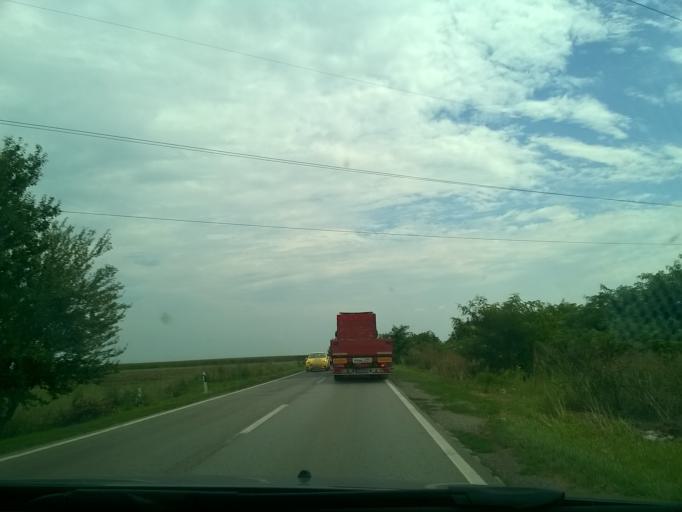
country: RS
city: Klek
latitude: 45.3837
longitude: 20.4459
